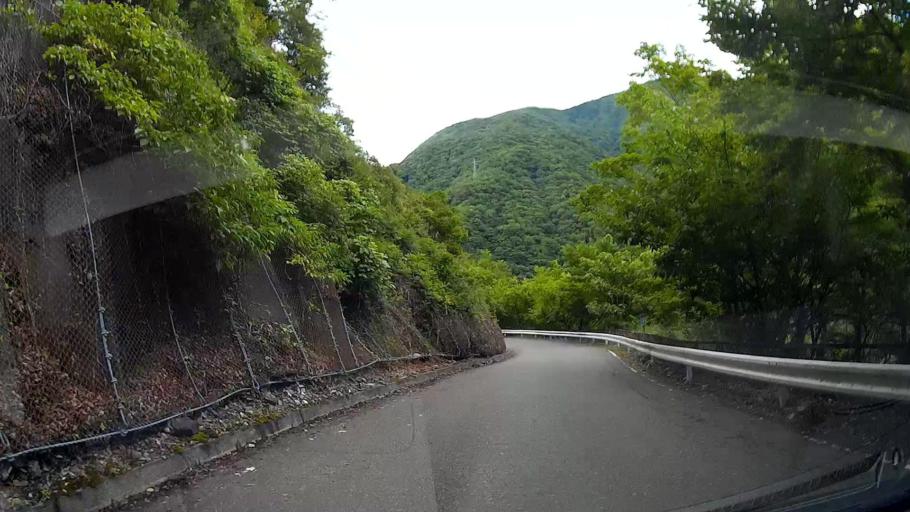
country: JP
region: Shizuoka
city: Shizuoka-shi
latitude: 35.3175
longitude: 138.1825
